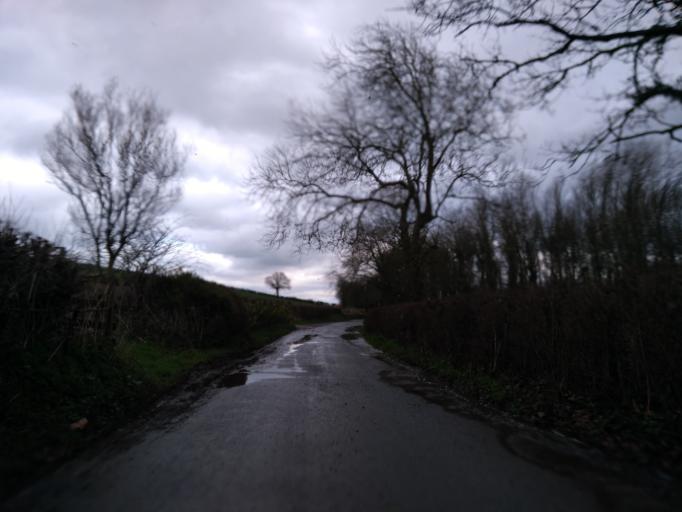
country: GB
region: England
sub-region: Devon
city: Crediton
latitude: 50.7912
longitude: -3.6251
